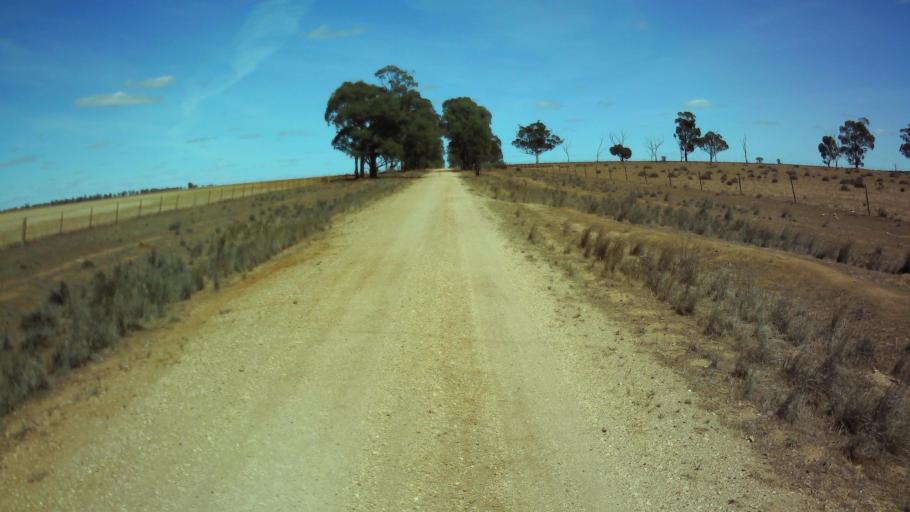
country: AU
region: New South Wales
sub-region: Weddin
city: Grenfell
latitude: -33.7273
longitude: 147.8839
